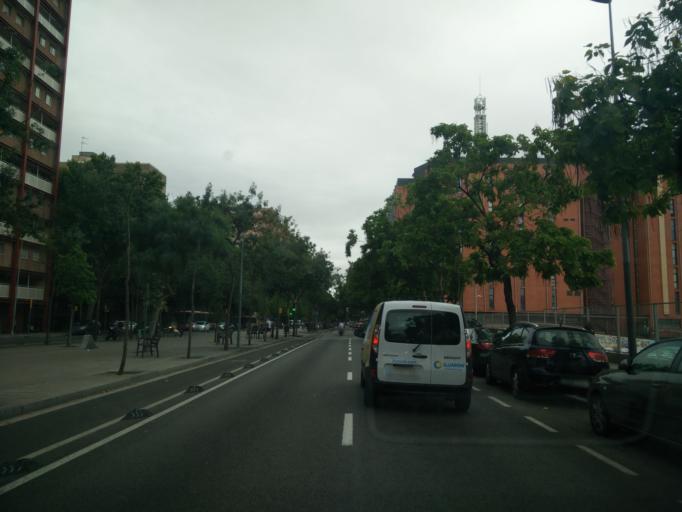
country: ES
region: Catalonia
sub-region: Provincia de Barcelona
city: Sant Marti
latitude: 41.4245
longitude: 2.2078
